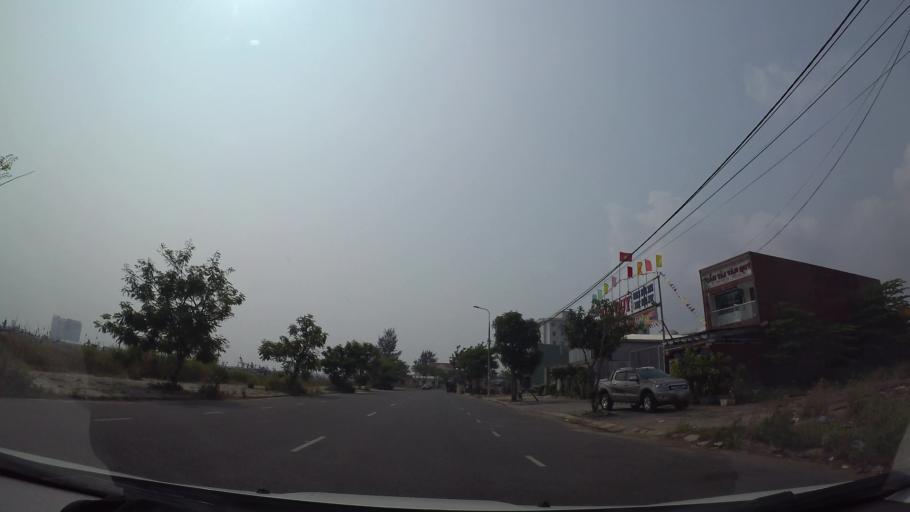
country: VN
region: Da Nang
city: Da Nang
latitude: 16.1013
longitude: 108.2346
